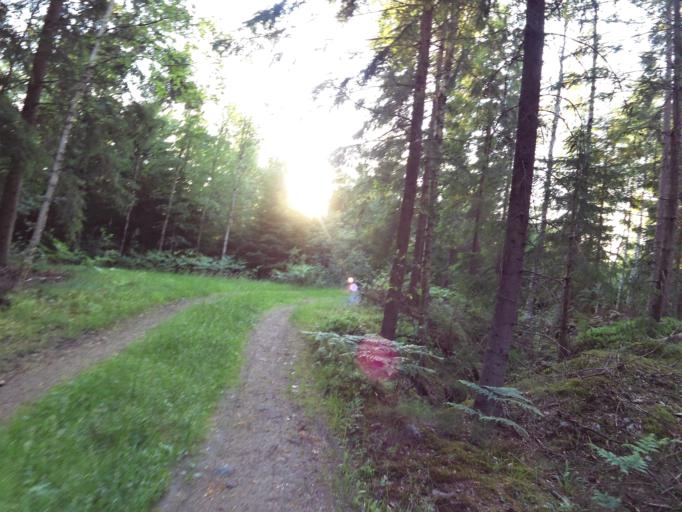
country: SE
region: Blekinge
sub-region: Olofstroms Kommun
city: Olofstroem
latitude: 56.4153
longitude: 14.5549
